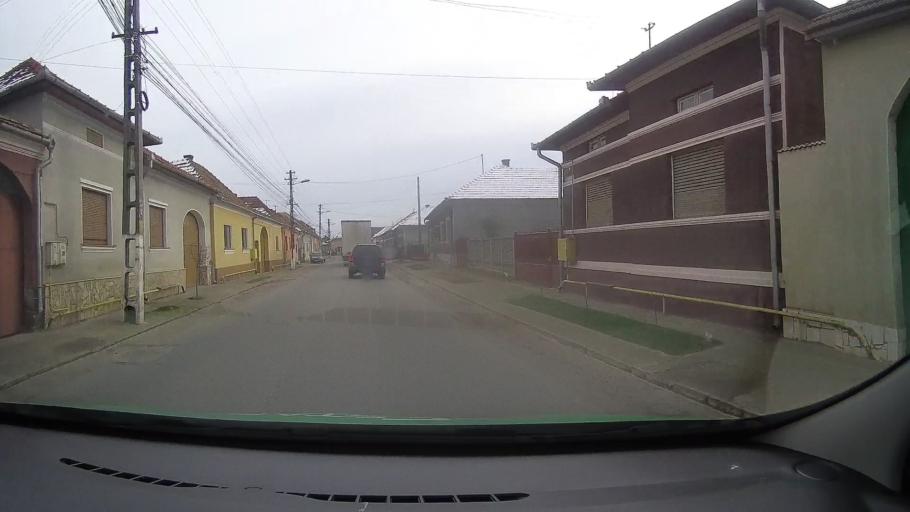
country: RO
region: Hunedoara
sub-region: Comuna Geoagiu
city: Geoagiu
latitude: 45.9107
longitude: 23.2067
